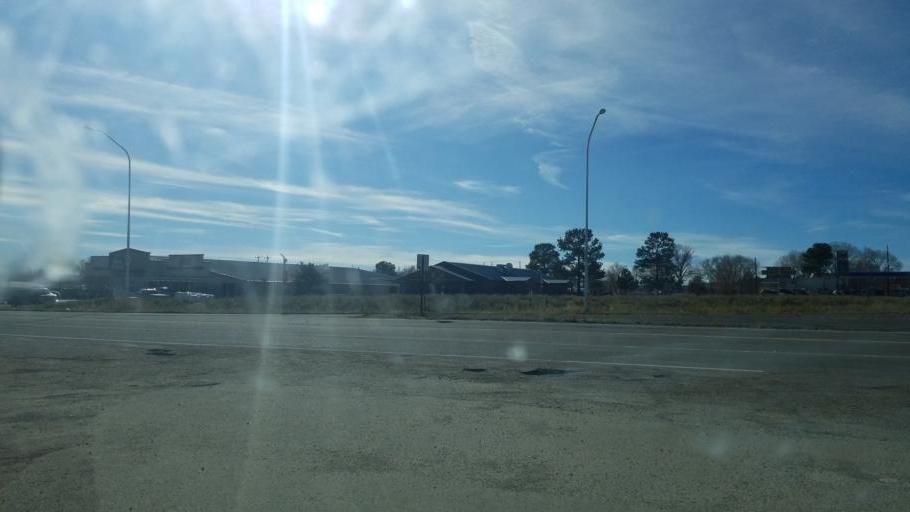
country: US
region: New Mexico
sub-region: Rio Arriba County
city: Chama
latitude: 36.8832
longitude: -106.5848
